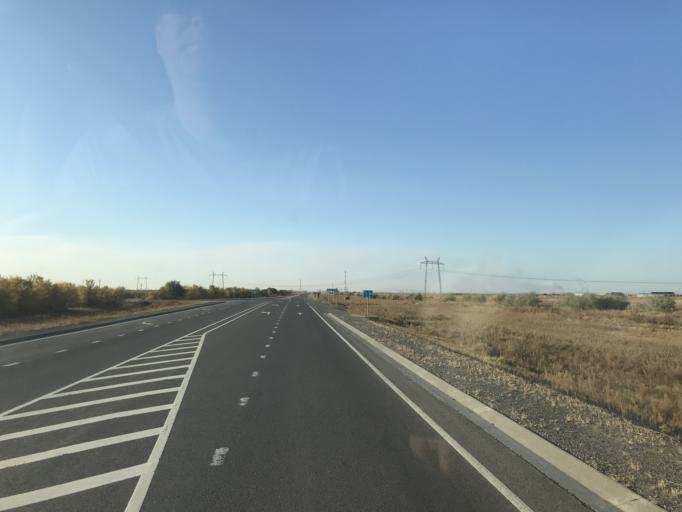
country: KZ
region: Pavlodar
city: Pavlodar
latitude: 52.0871
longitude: 77.1276
